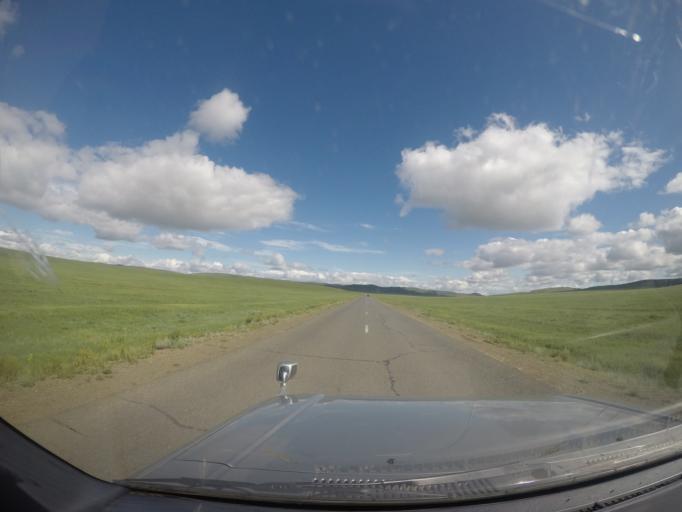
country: MN
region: Hentiy
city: Bayanbulag
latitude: 47.4458
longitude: 109.7088
